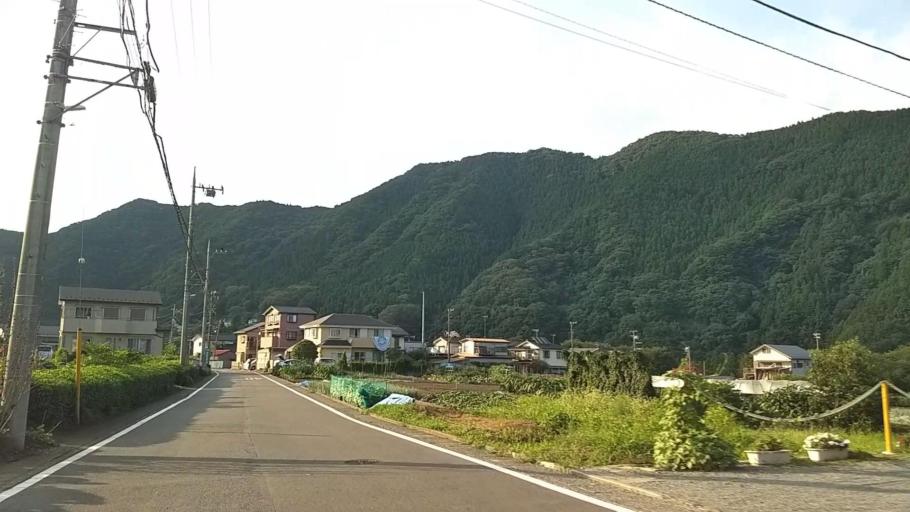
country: JP
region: Tokyo
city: Hachioji
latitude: 35.5950
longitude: 139.2473
